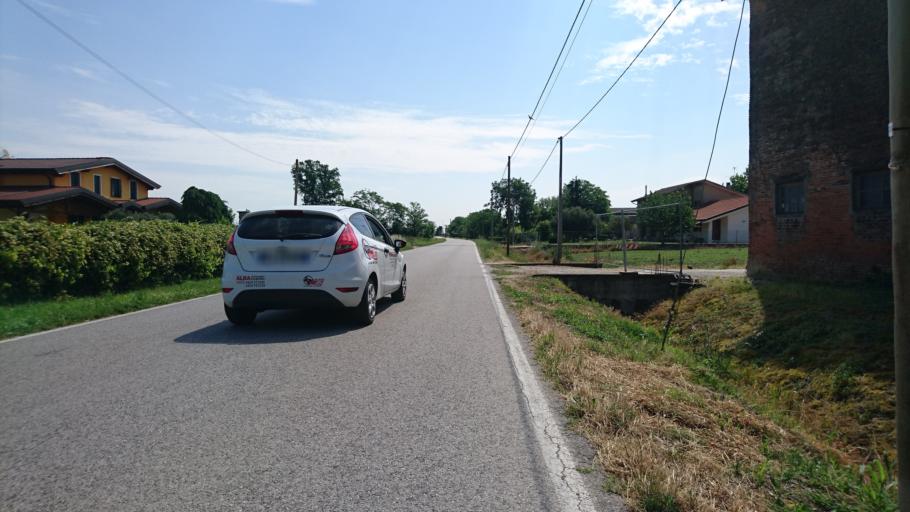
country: IT
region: Veneto
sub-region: Provincia di Padova
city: Santa Margherita d'Adige
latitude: 45.1920
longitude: 11.5503
